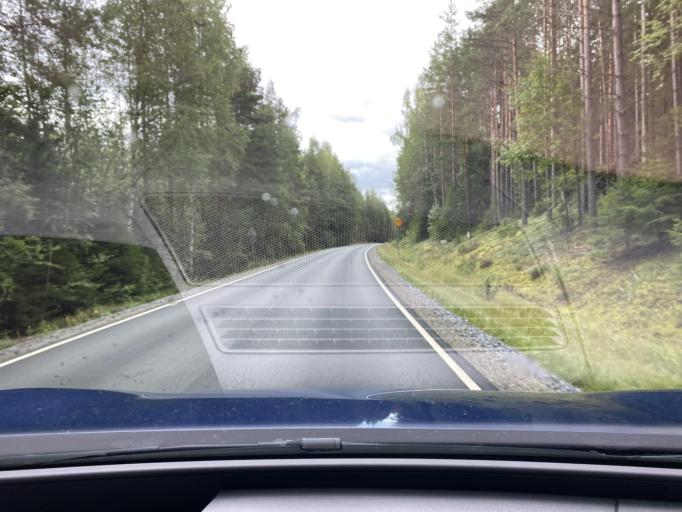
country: FI
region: Pirkanmaa
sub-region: Lounais-Pirkanmaa
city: Vammala
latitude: 61.3001
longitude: 22.9807
